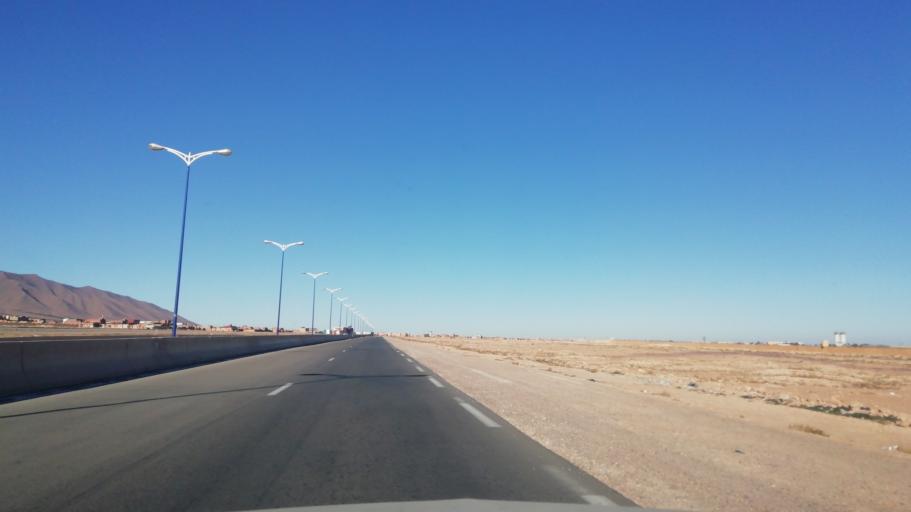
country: DZ
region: Wilaya de Naama
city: Naama
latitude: 33.5210
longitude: -0.2758
